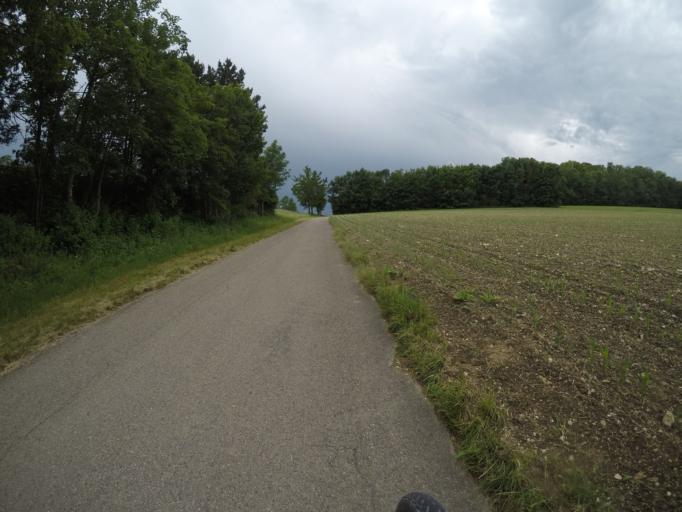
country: DE
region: Baden-Wuerttemberg
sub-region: Tuebingen Region
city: Ulm
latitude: 48.4228
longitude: 9.9830
